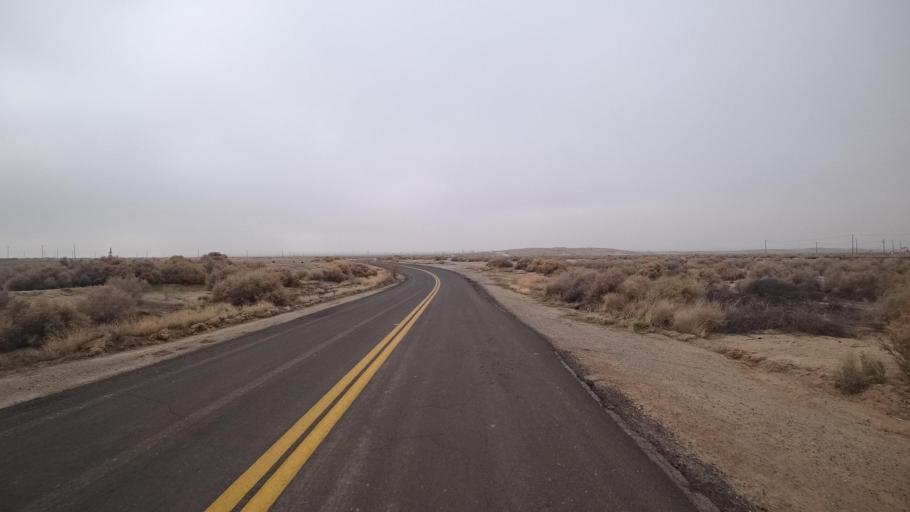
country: US
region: California
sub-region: Kern County
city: Maricopa
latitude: 35.0757
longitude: -119.3512
